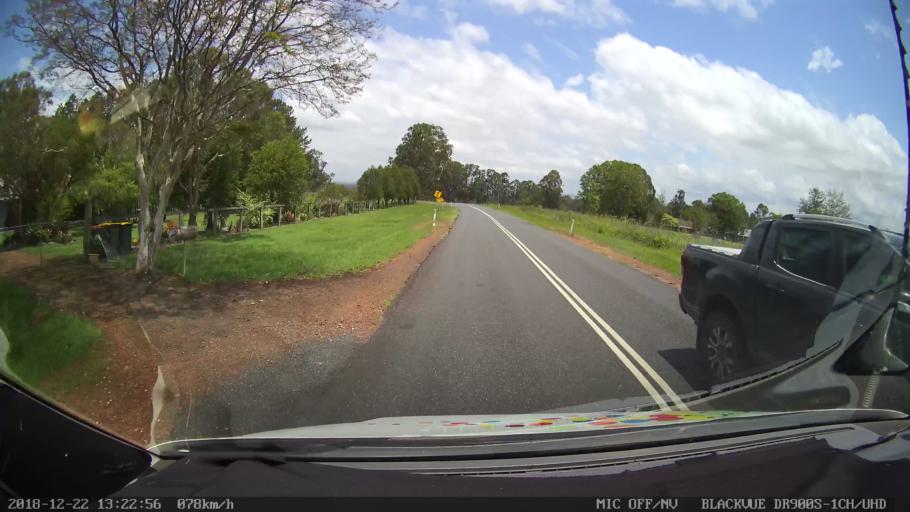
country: AU
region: New South Wales
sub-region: Clarence Valley
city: Coutts Crossing
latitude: -29.7926
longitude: 152.9098
